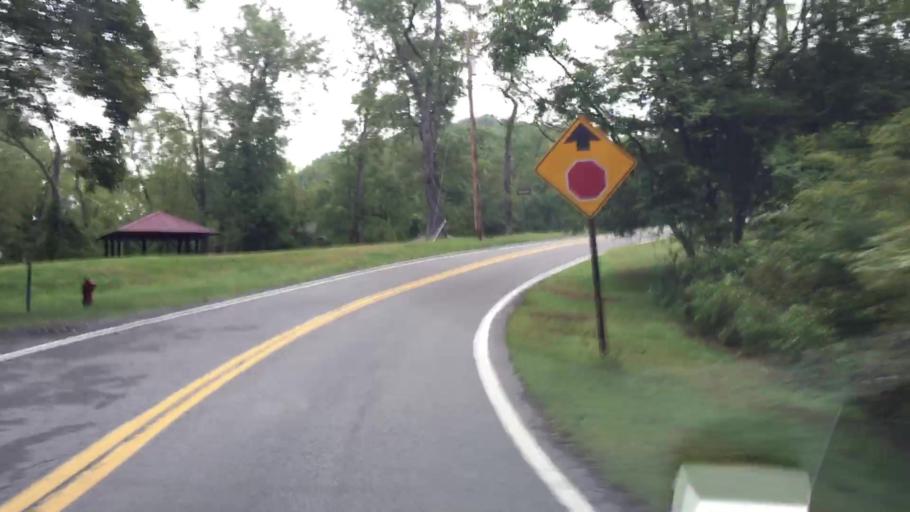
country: US
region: Pennsylvania
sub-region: Allegheny County
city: Gibsonia
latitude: 40.5920
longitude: -79.9985
